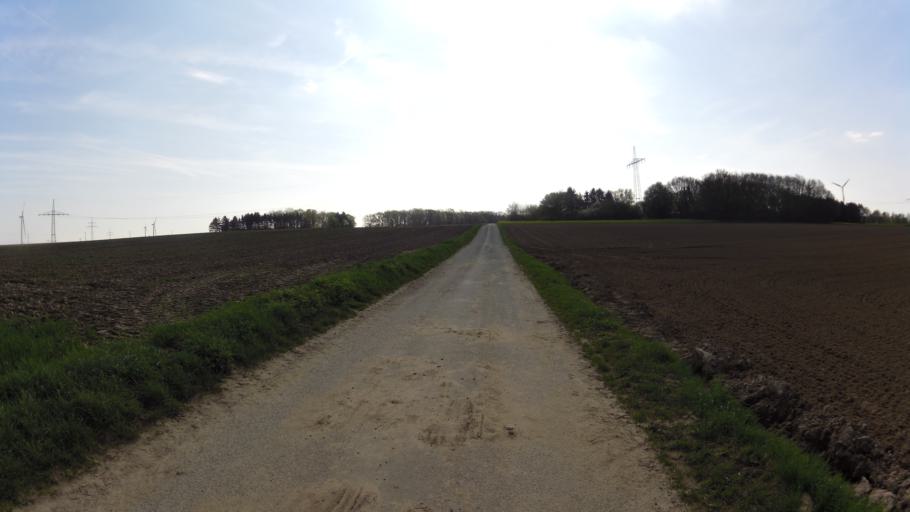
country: DE
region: North Rhine-Westphalia
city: Geilenkirchen
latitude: 50.9991
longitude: 6.0665
